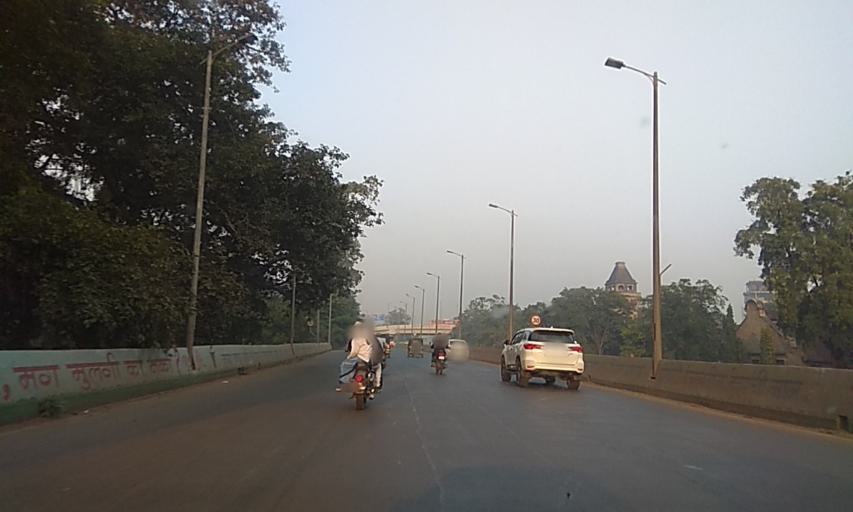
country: IN
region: Maharashtra
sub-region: Pune Division
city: Shivaji Nagar
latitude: 18.5297
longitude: 73.8573
